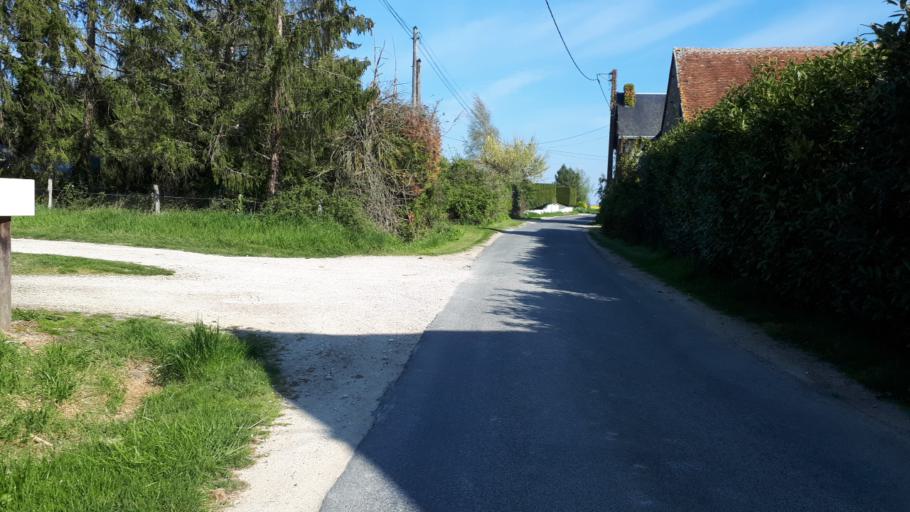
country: FR
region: Centre
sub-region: Departement du Loir-et-Cher
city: Contres
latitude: 47.3824
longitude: 1.3900
